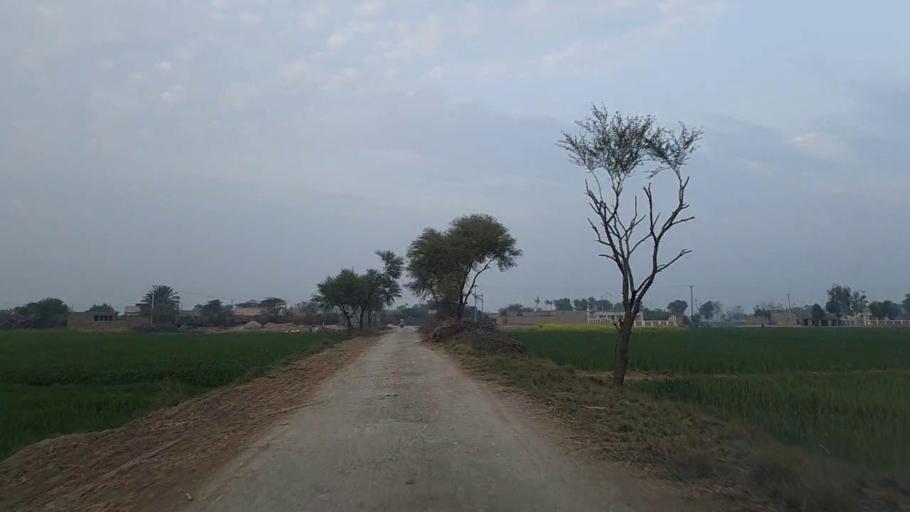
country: PK
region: Sindh
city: Jam Sahib
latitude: 26.2973
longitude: 68.5935
